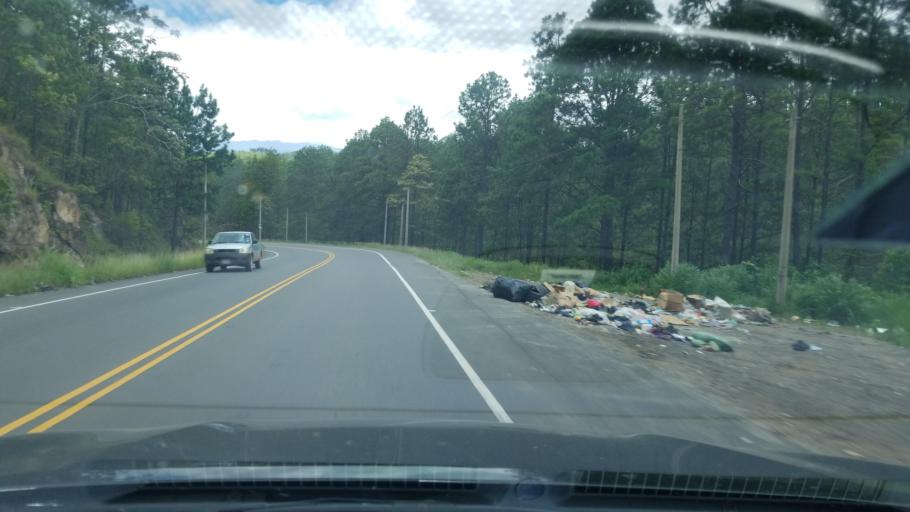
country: HN
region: Francisco Morazan
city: Talanga
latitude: 14.3528
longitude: -87.1590
